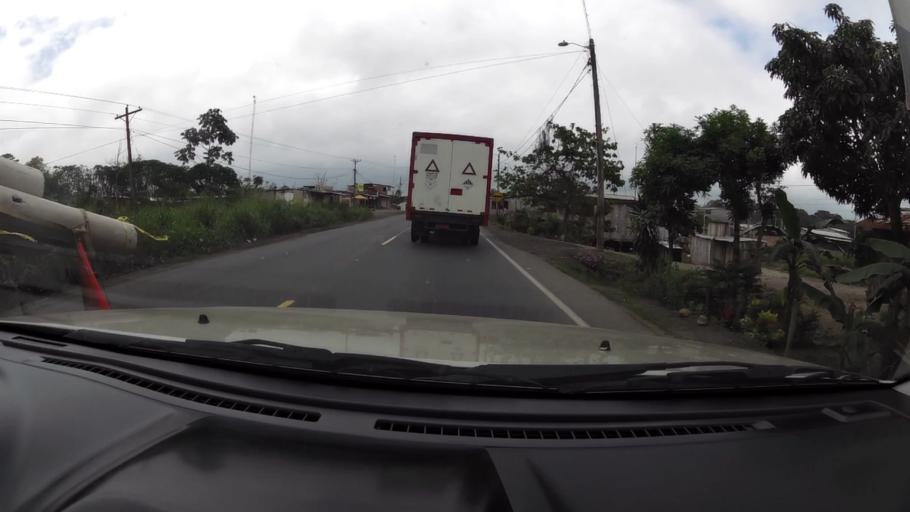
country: EC
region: Guayas
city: Balao
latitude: -2.9032
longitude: -79.7063
